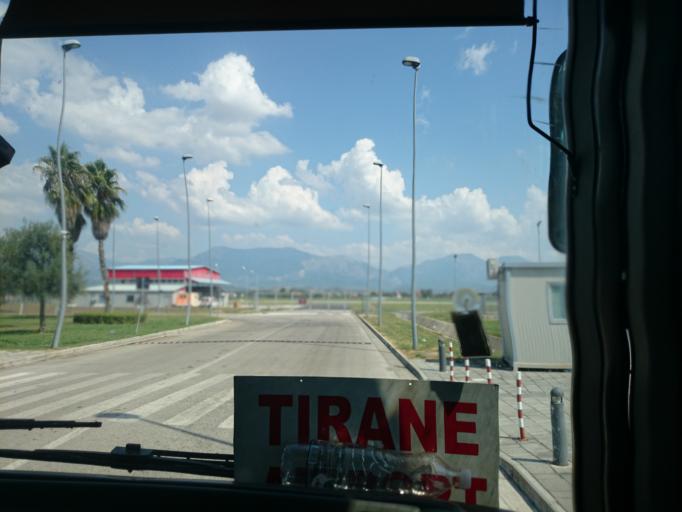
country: AL
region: Tirane
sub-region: Rrethi i Tiranes
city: Preze
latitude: 41.4169
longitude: 19.7136
